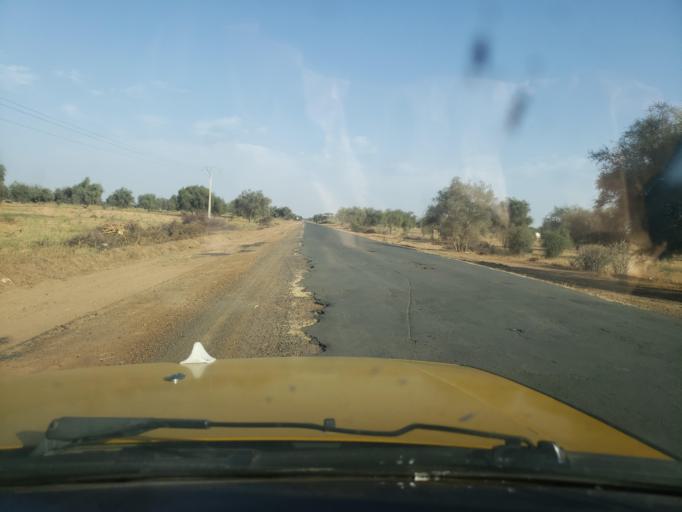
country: SN
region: Louga
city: Louga
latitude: 15.5025
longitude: -15.9455
